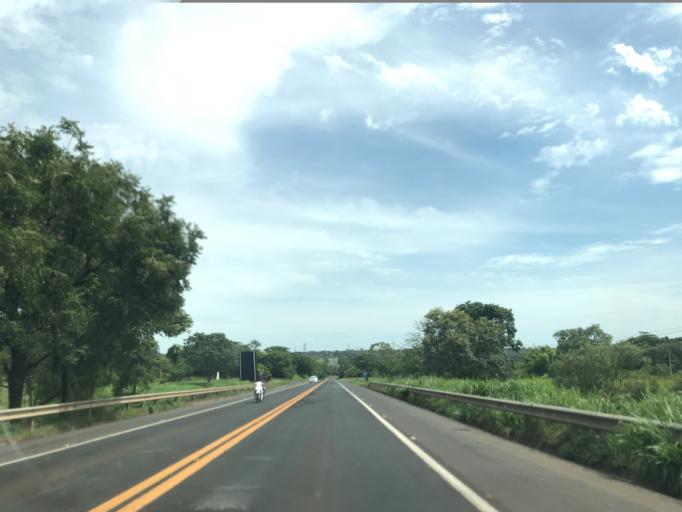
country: BR
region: Sao Paulo
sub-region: Nova Granada
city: Nova Granada
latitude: -20.3155
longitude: -49.2097
